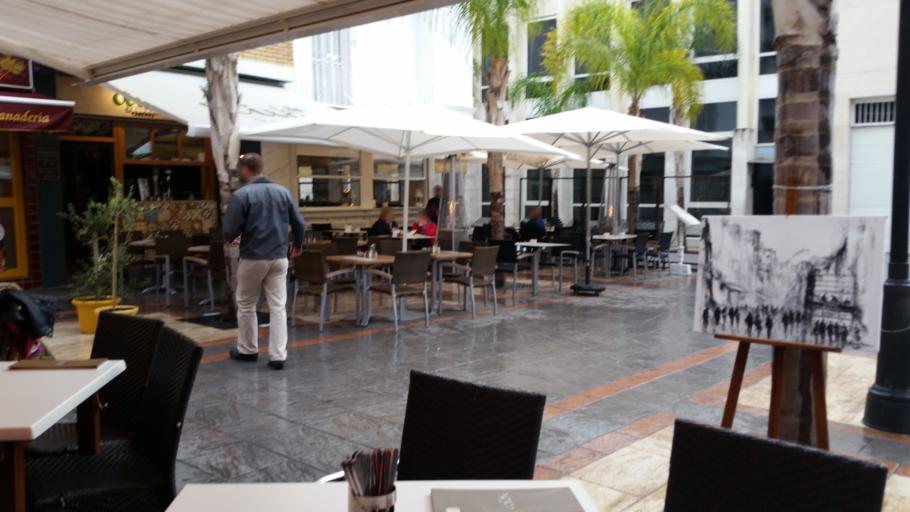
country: ES
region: Andalusia
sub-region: Provincia de Malaga
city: Fuengirola
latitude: 36.5381
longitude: -4.6235
